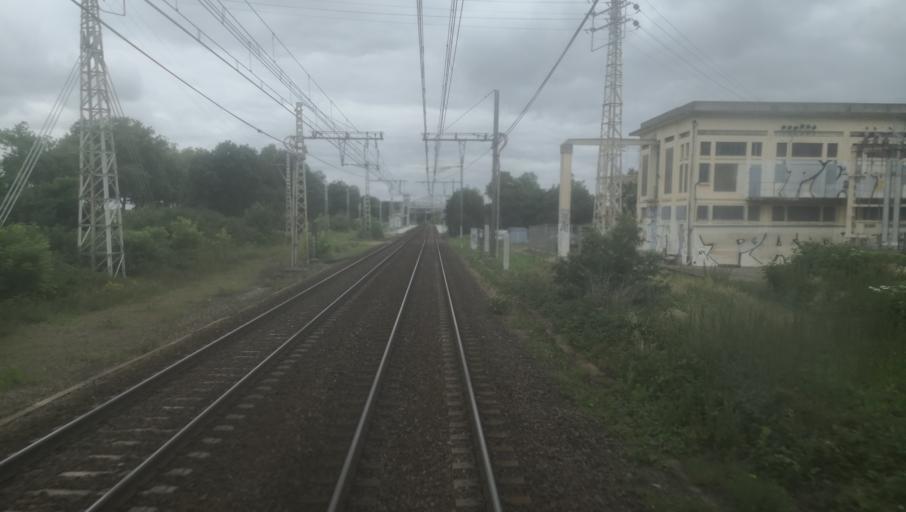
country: FR
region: Midi-Pyrenees
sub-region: Departement de la Haute-Garonne
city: Saint-Jory
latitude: 43.7366
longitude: 1.3730
